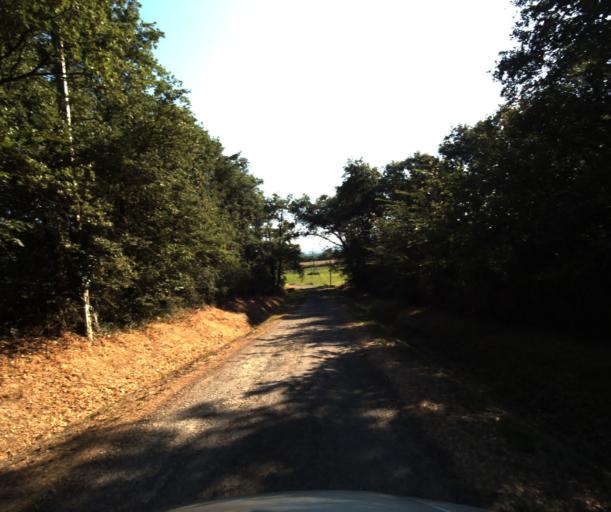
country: FR
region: Midi-Pyrenees
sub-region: Departement de la Haute-Garonne
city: Eaunes
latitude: 43.4357
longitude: 1.3696
